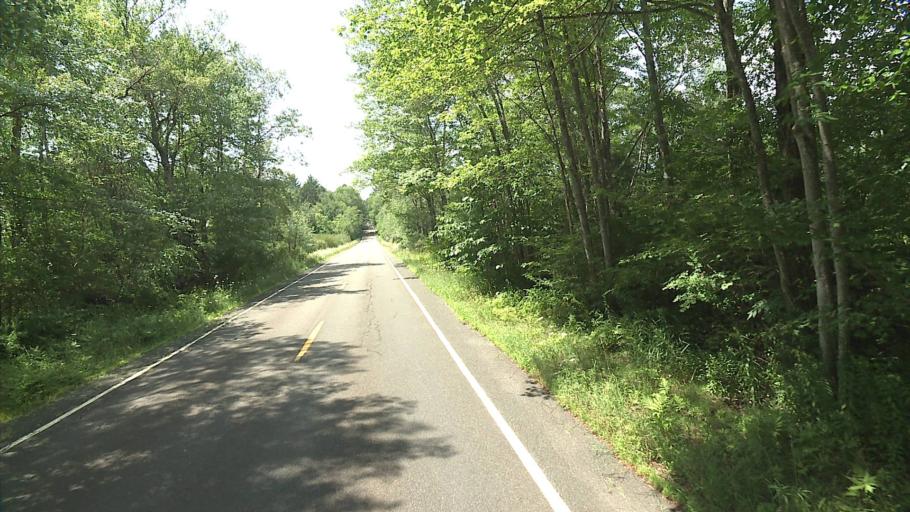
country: US
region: Connecticut
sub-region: Litchfield County
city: Winsted
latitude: 41.9891
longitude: -73.0997
